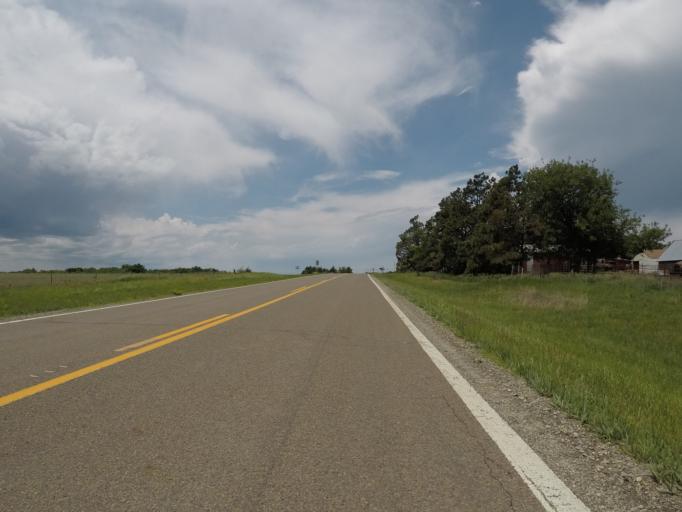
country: US
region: Kansas
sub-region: Wabaunsee County
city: Alma
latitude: 38.8550
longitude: -96.4083
